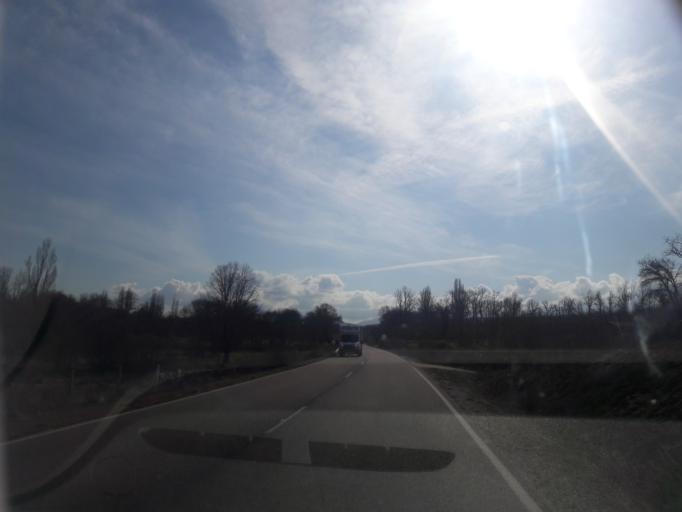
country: ES
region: Castille and Leon
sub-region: Provincia de Salamanca
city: Valdehijaderos
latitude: 40.4213
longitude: -5.8650
